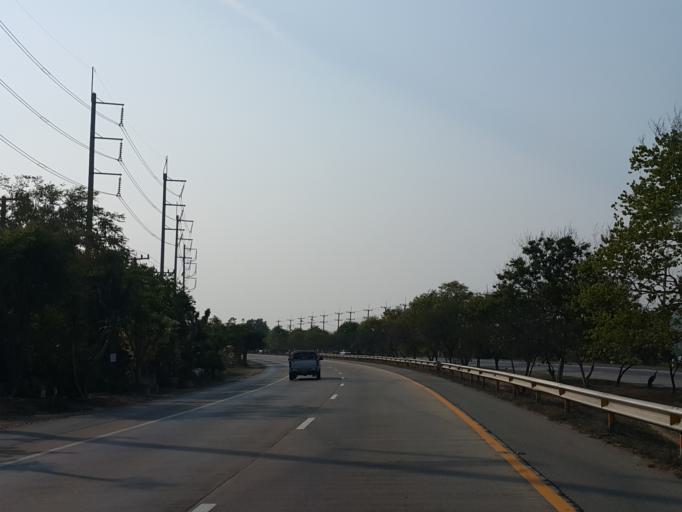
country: TH
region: Suphan Buri
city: Doembang Nangbuat
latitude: 14.8401
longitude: 100.1071
